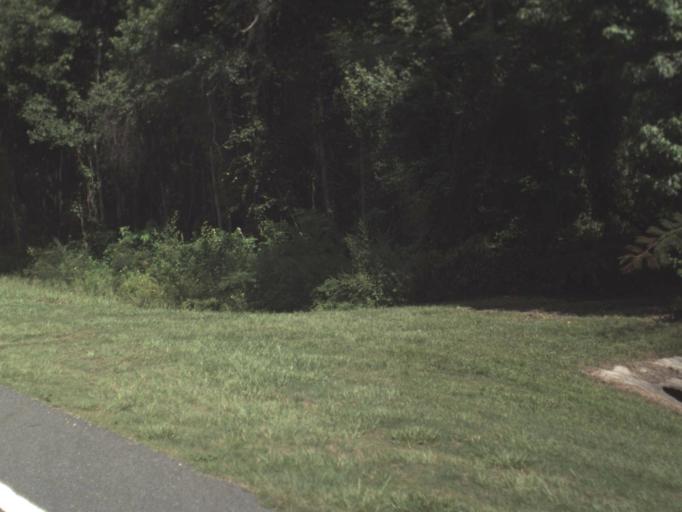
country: US
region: Florida
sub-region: Alachua County
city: Alachua
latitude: 29.8401
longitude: -82.3639
